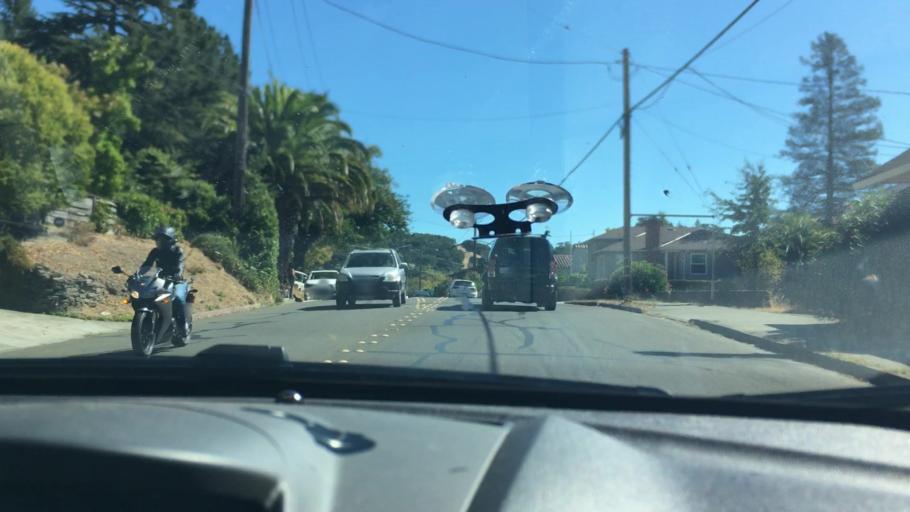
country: US
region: California
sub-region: Marin County
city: Fairfax
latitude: 37.9866
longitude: -122.5798
